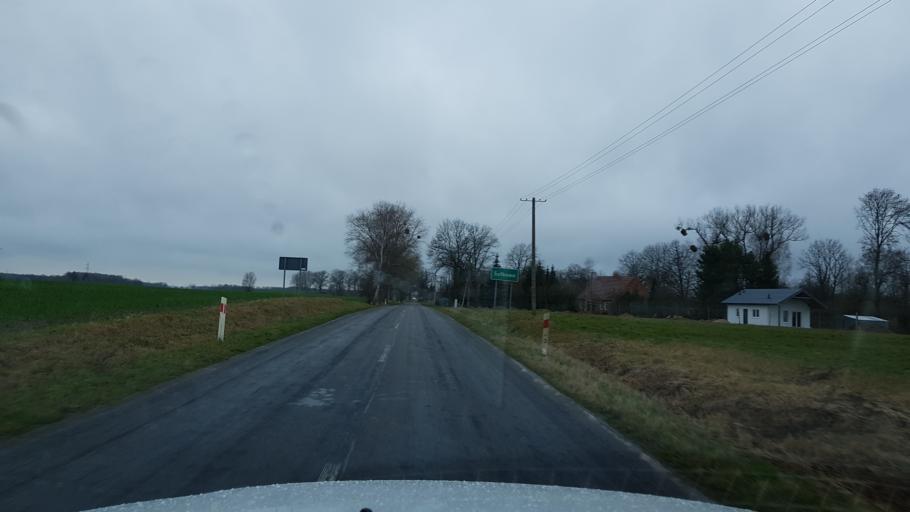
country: PL
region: West Pomeranian Voivodeship
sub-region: Powiat lobeski
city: Radowo Male
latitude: 53.6130
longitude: 15.4681
